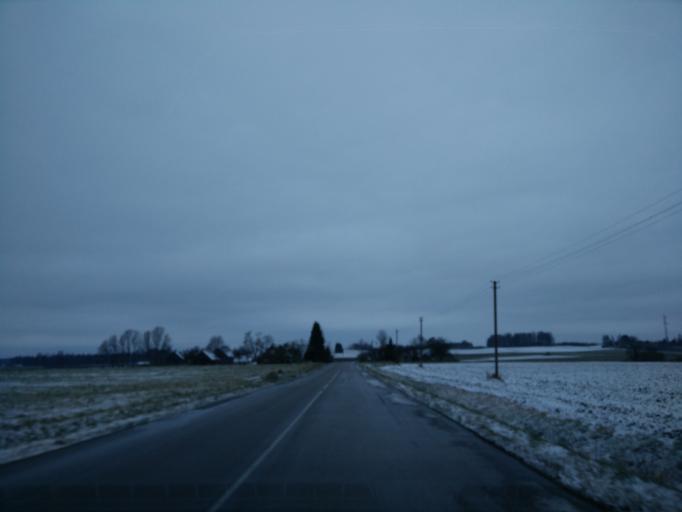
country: LT
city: Tytuveneliai
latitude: 55.5114
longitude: 23.2833
